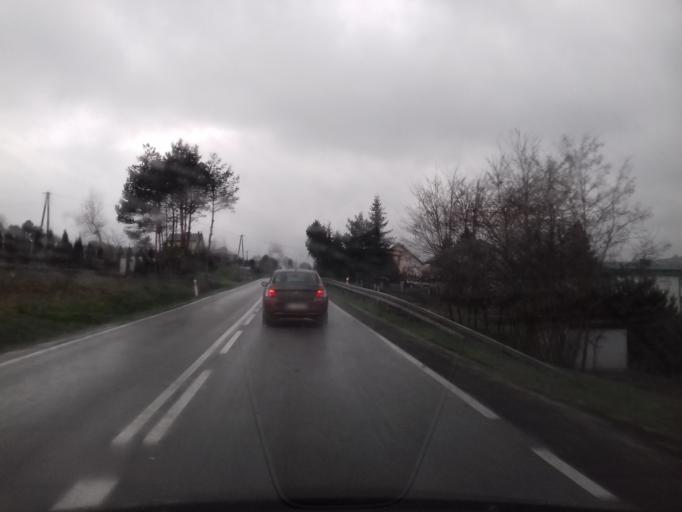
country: PL
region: Lesser Poland Voivodeship
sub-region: Powiat nowosadecki
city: Chelmiec
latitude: 49.6331
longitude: 20.6371
